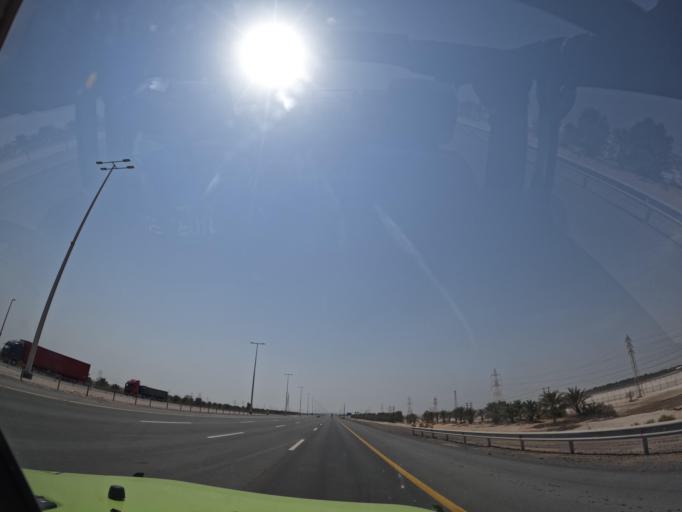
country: AE
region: Abu Dhabi
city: Abu Dhabi
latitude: 24.1817
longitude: 54.3753
